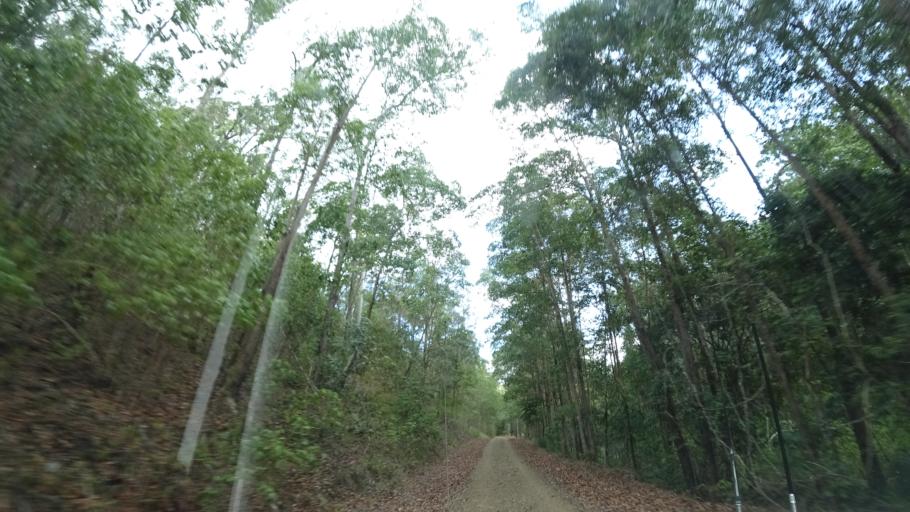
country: AU
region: Queensland
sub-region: Moreton Bay
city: Highvale
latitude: -27.3504
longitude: 152.7264
